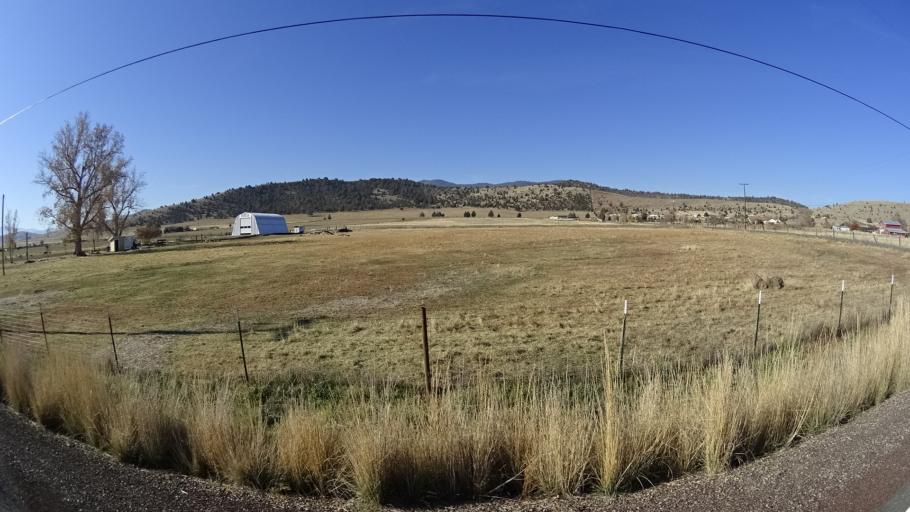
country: US
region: California
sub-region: Siskiyou County
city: Montague
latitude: 41.6324
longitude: -122.5300
